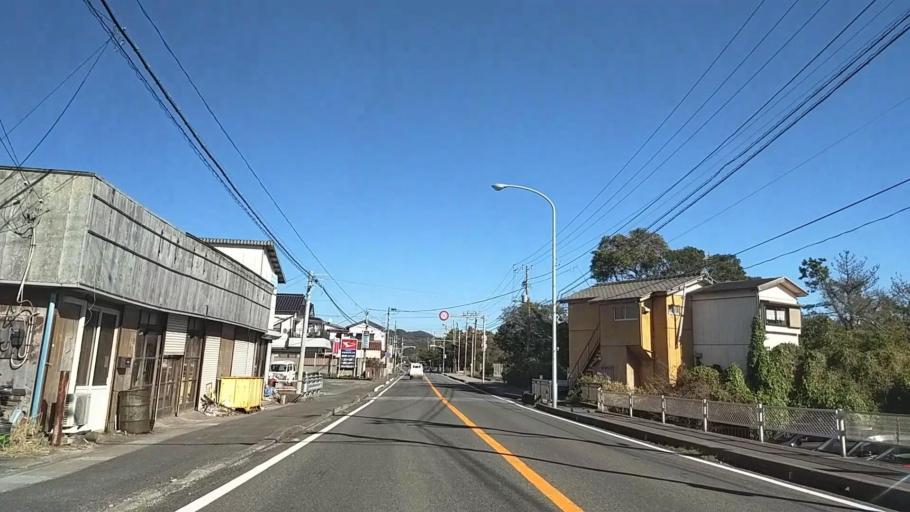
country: JP
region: Chiba
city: Kawaguchi
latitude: 35.0417
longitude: 140.0206
